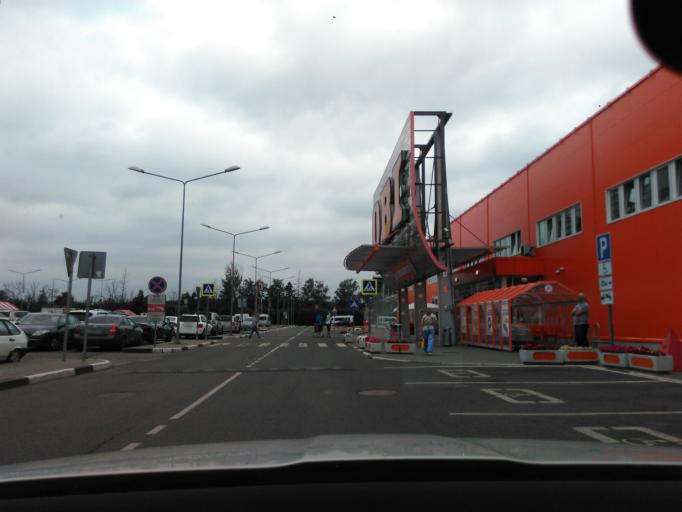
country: RU
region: Moscow
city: Khimki
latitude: 55.9117
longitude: 37.3930
